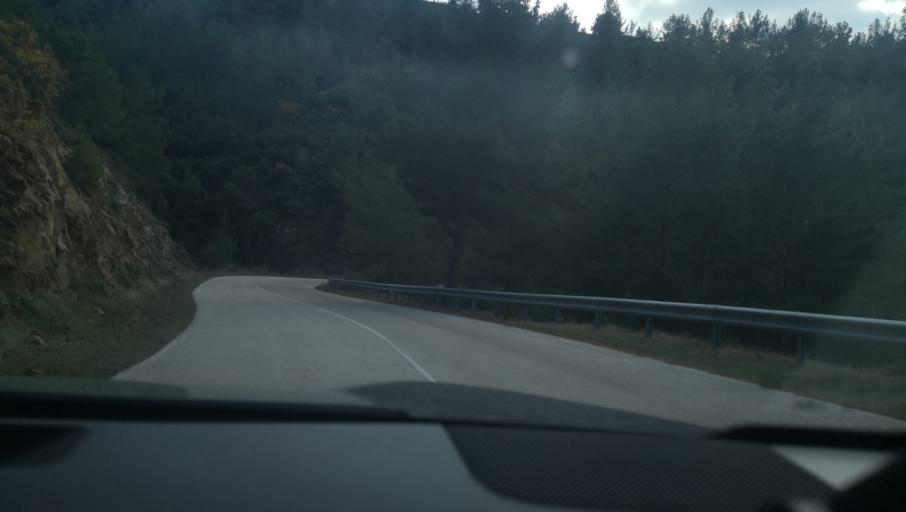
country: CY
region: Lefkosia
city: Lefka
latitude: 35.0527
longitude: 32.7476
